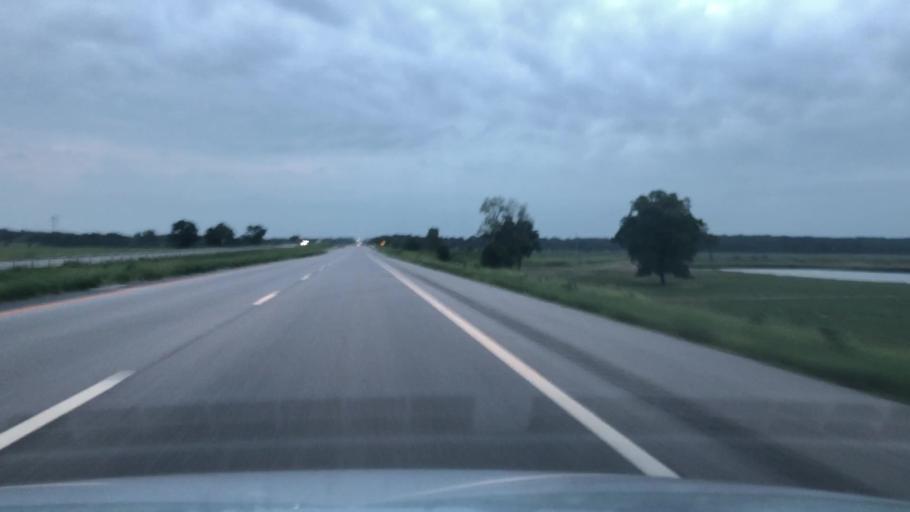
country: US
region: Oklahoma
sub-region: Washington County
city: Bartlesville
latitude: 36.6517
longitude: -95.9353
